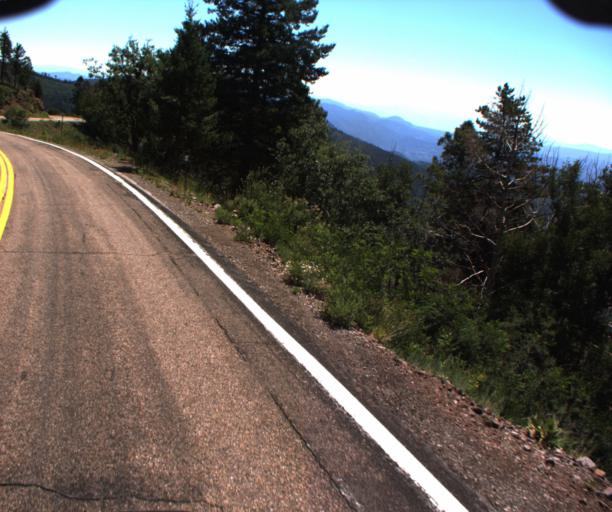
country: US
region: Arizona
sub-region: Greenlee County
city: Morenci
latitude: 33.5665
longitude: -109.3520
